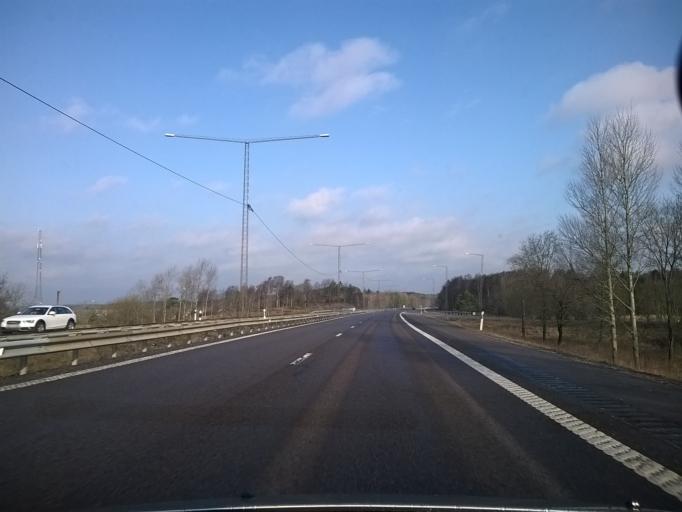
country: SE
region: Vaestra Goetaland
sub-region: Kungalvs Kommun
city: Kode
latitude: 57.9441
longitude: 11.8577
